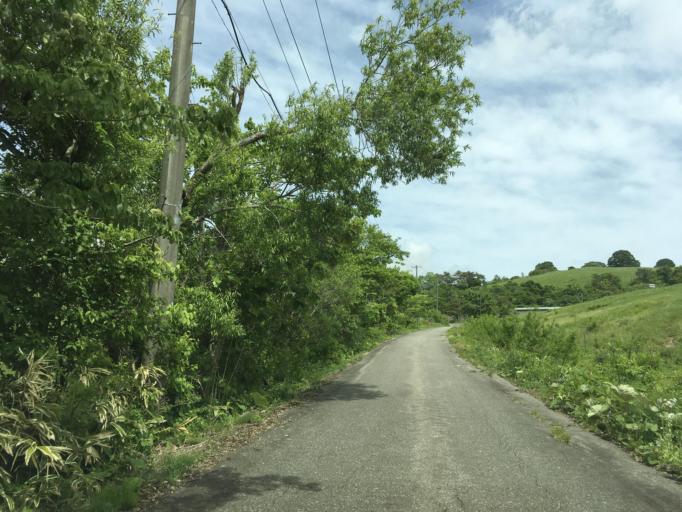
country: JP
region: Iwate
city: Mizusawa
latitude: 39.1362
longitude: 141.3086
